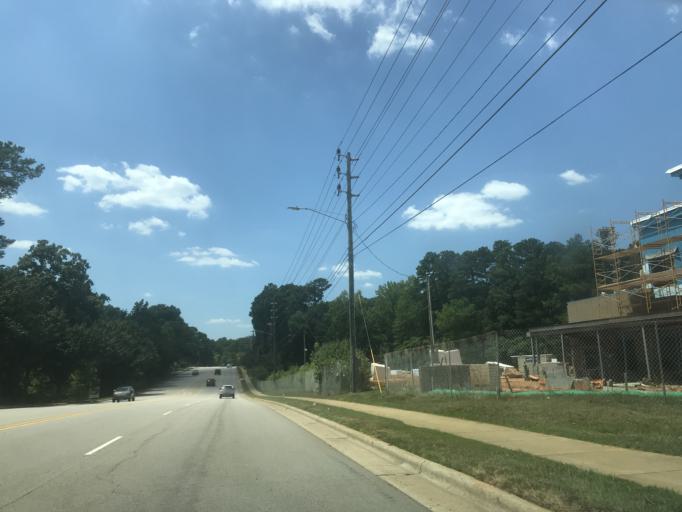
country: US
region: North Carolina
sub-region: Wake County
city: Cary
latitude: 35.7651
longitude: -78.7523
